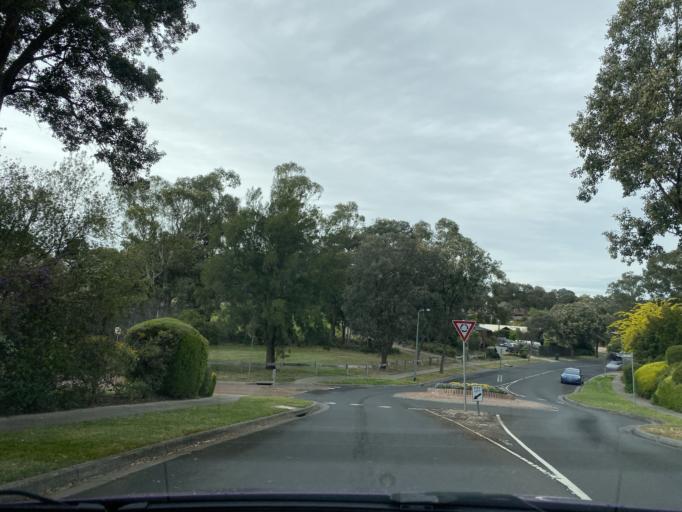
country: AU
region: Victoria
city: Saint Helena
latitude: -37.6884
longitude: 145.1360
